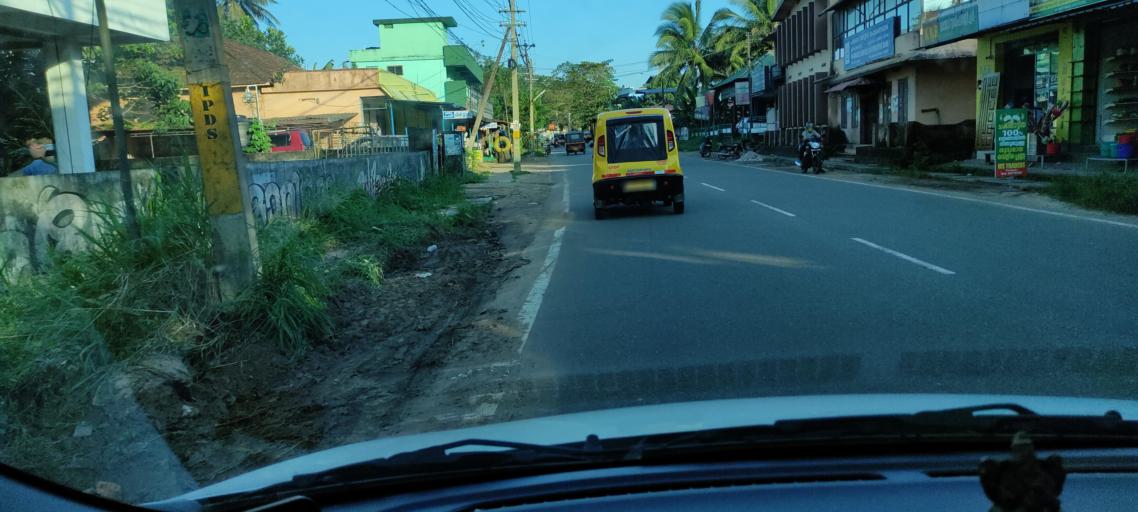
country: IN
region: Kerala
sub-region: Pattanamtitta
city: Adur
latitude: 9.1490
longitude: 76.7564
